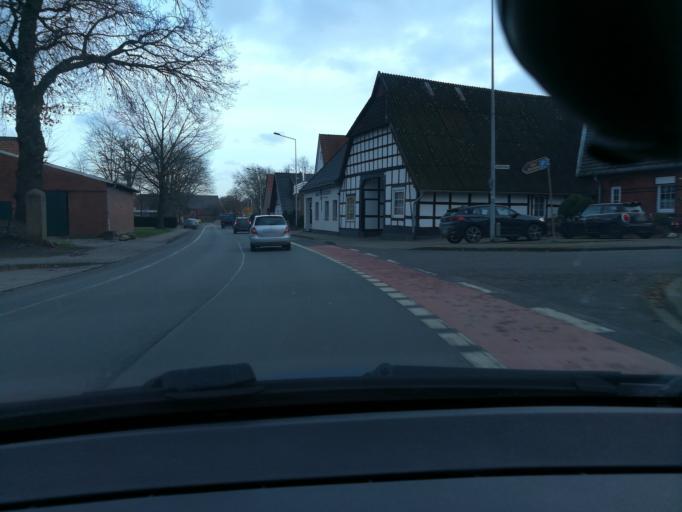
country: DE
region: North Rhine-Westphalia
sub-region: Regierungsbezirk Detmold
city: Hille
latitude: 52.3146
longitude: 8.8165
